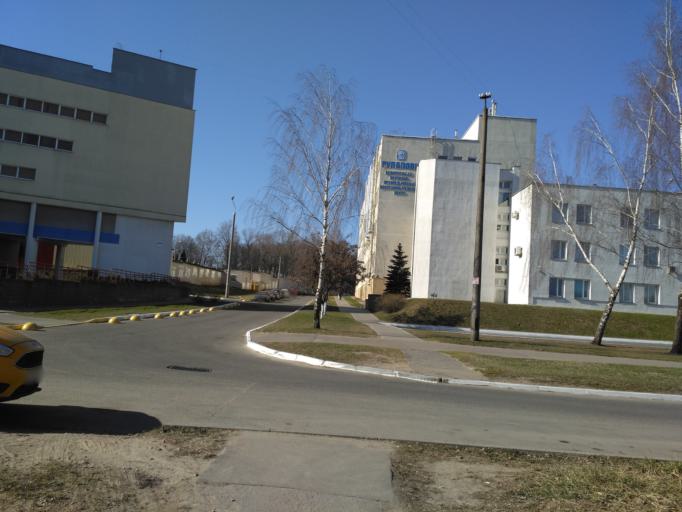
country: BY
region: Minsk
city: Minsk
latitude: 53.9049
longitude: 27.5082
